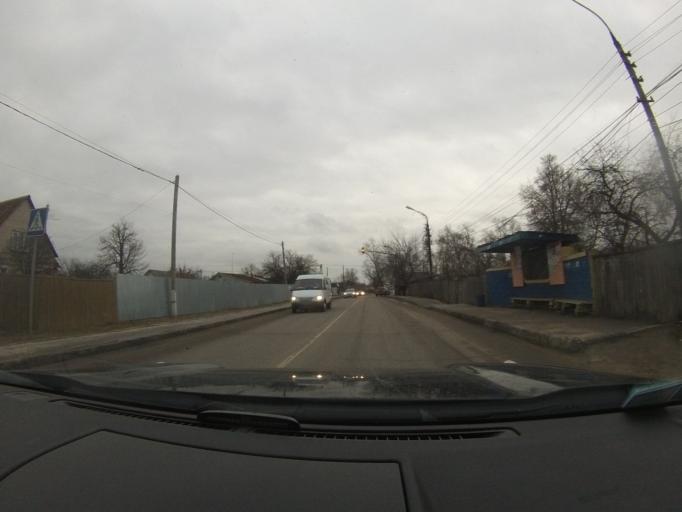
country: RU
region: Moskovskaya
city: Lopatinskiy
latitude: 55.3277
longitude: 38.7118
